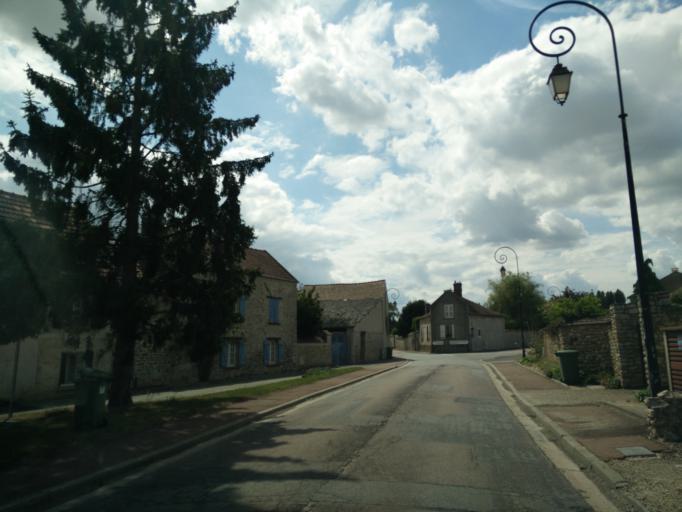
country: FR
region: Ile-de-France
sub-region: Departement des Yvelines
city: Guerville
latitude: 48.9099
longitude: 1.7319
